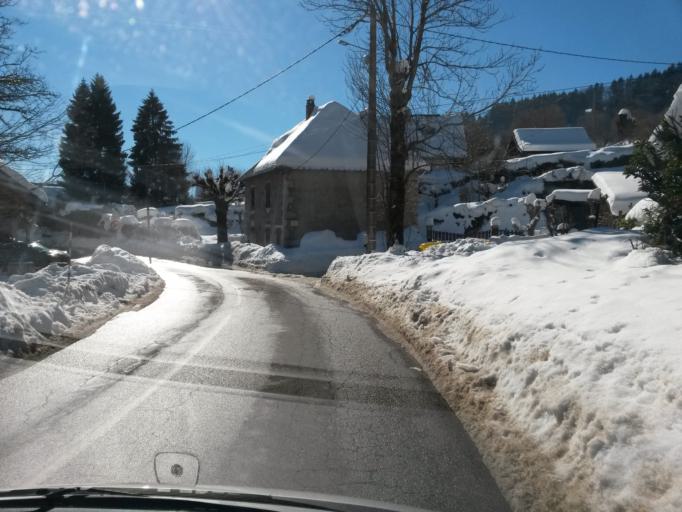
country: FR
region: Rhone-Alpes
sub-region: Departement de l'Isere
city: Saint-Hilaire
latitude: 45.3167
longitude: 5.8880
